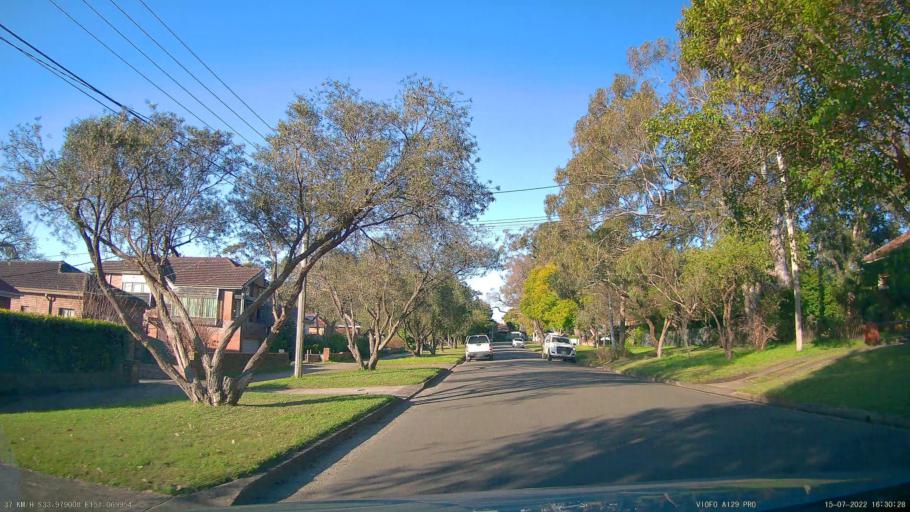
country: AU
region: New South Wales
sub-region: Hurstville
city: Oatley
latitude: -33.9790
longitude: 151.0702
